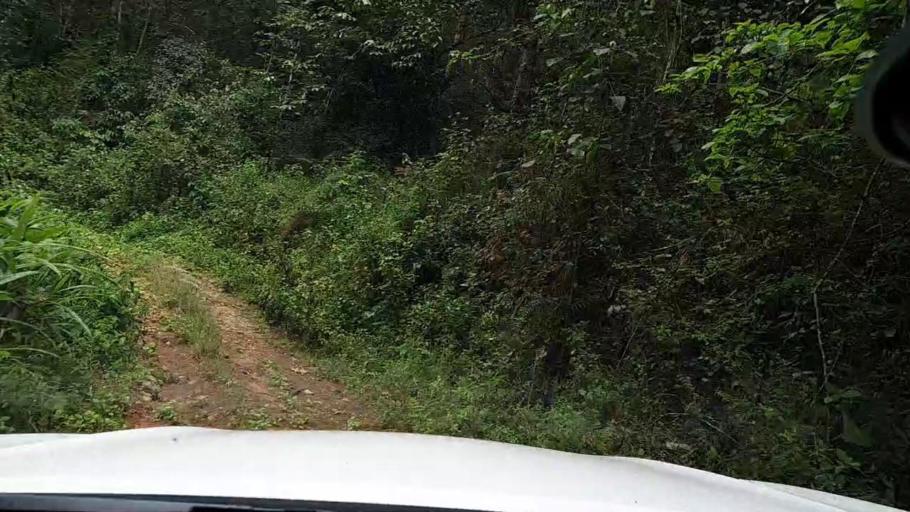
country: RW
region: Western Province
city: Kibuye
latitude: -2.2893
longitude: 29.3054
